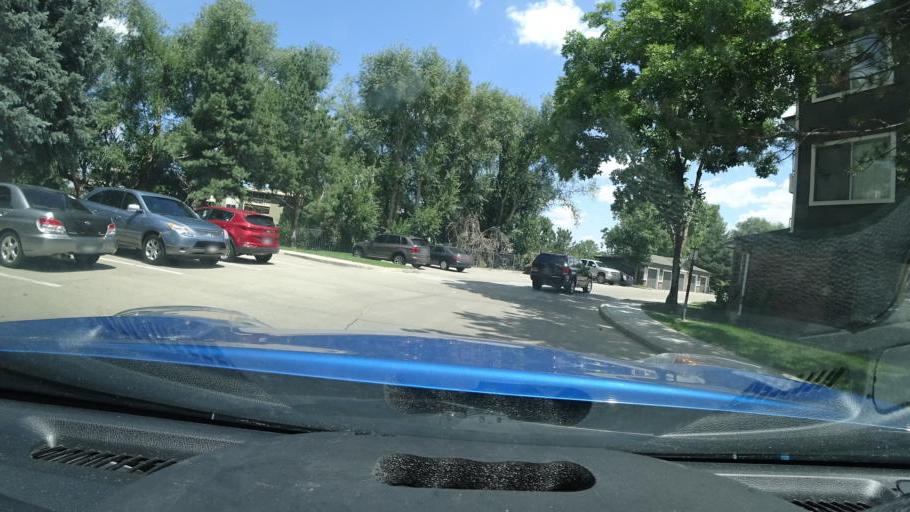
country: US
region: Colorado
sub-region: Adams County
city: Aurora
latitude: 39.6998
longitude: -104.8782
